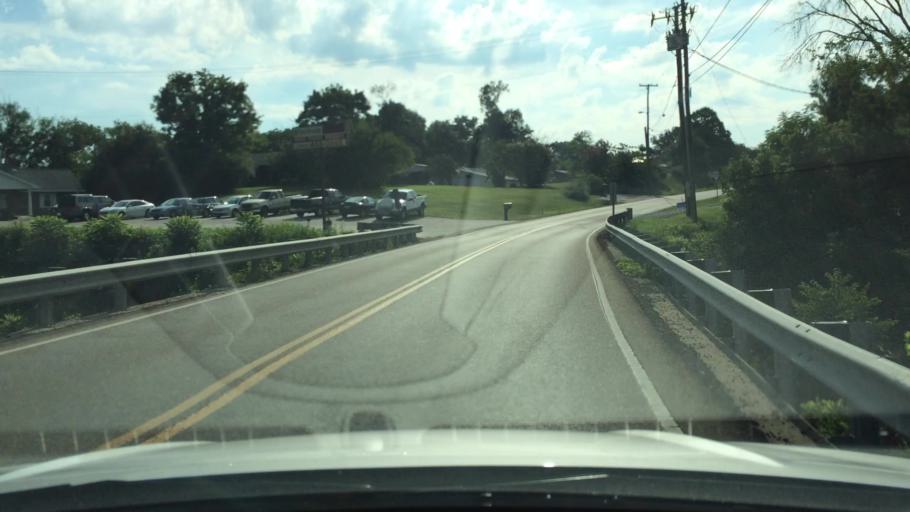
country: US
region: Tennessee
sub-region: Sevier County
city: Seymour
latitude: 35.9264
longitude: -83.6528
